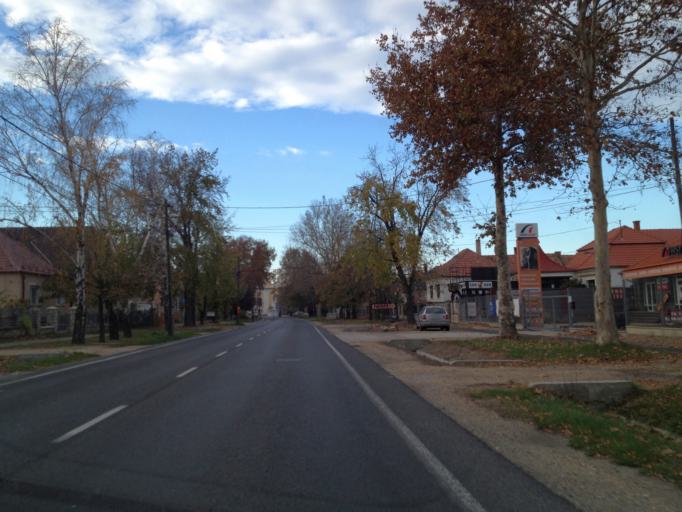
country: HU
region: Gyor-Moson-Sopron
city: Nyul
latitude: 47.5879
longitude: 17.6925
